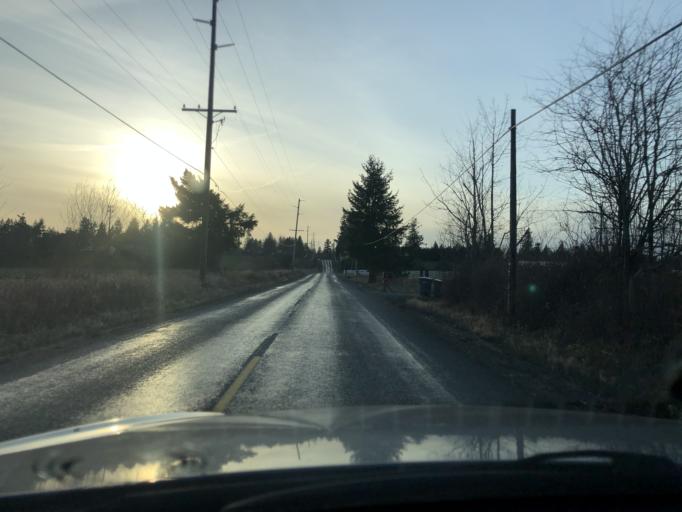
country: US
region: Washington
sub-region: Pierce County
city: Bonney Lake
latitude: 47.2211
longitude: -122.1332
